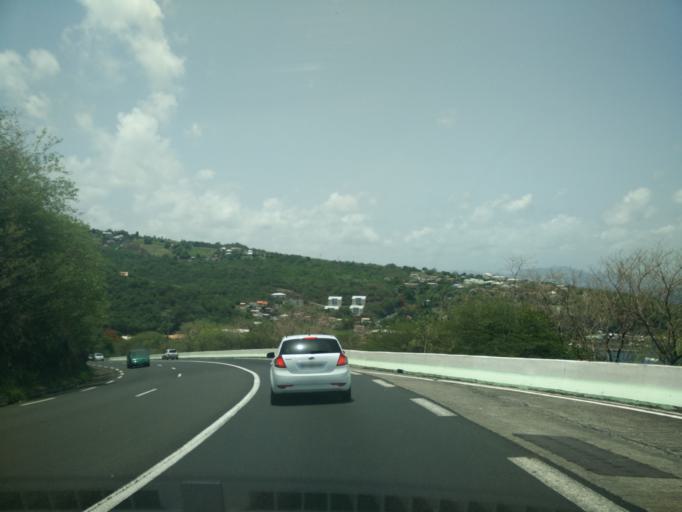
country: MQ
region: Martinique
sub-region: Martinique
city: Fort-de-France
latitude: 14.6473
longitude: -61.1417
